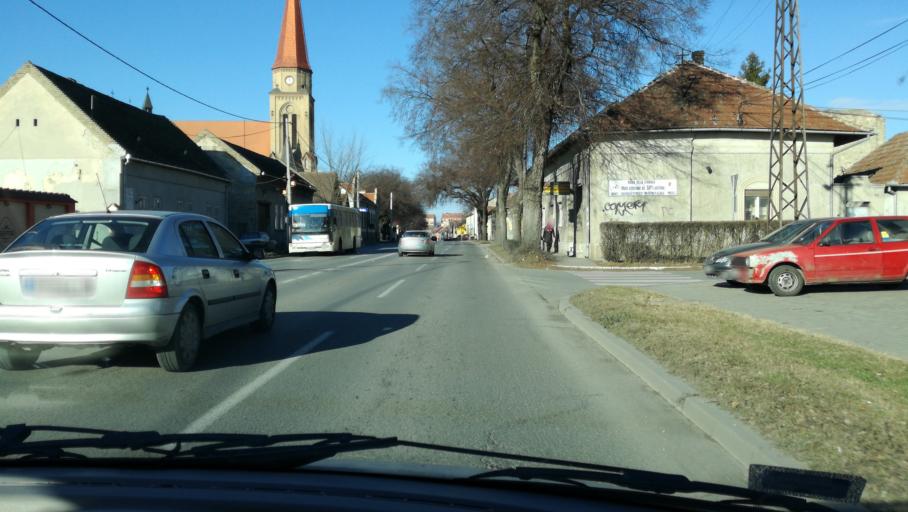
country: RS
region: Autonomna Pokrajina Vojvodina
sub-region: Severnobacki Okrug
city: Subotica
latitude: 46.0884
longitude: 19.6672
